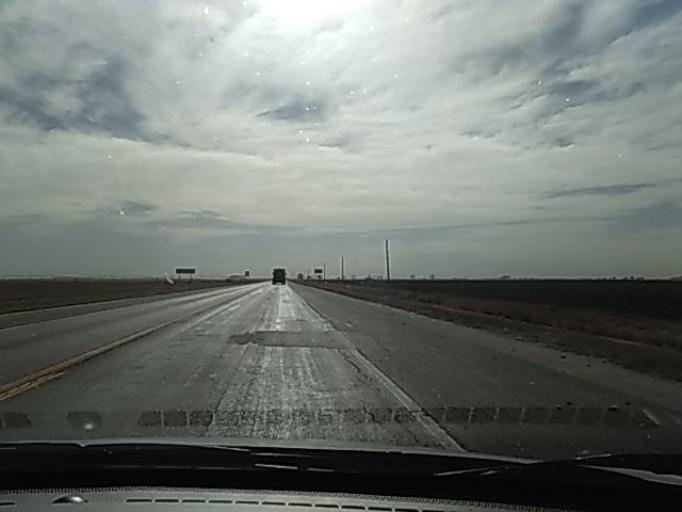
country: US
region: Nebraska
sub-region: Clay County
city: Clay Center
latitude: 40.4226
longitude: -98.0516
